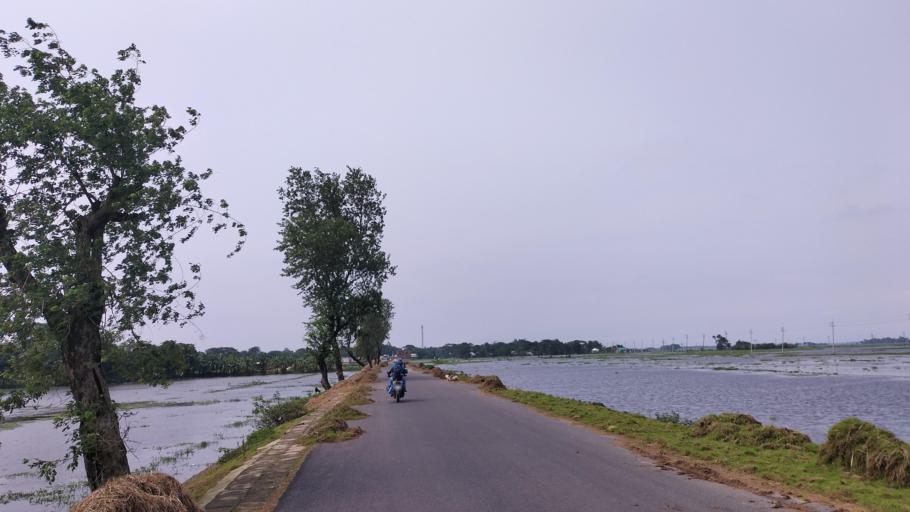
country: BD
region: Dhaka
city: Netrakona
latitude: 24.9627
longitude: 90.8337
